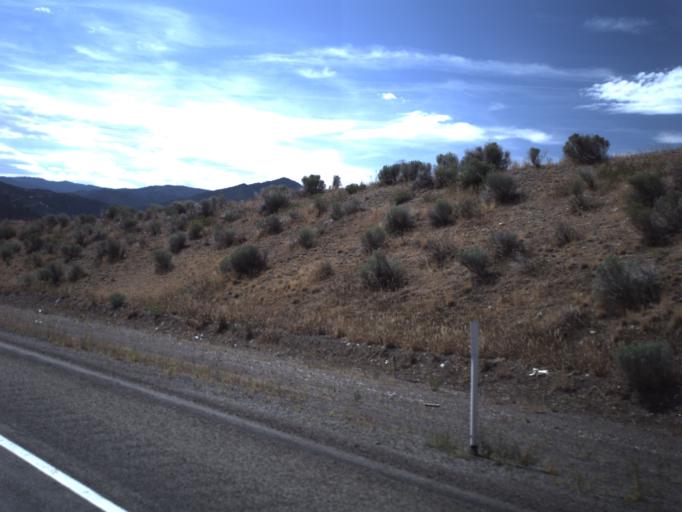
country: US
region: Utah
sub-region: Utah County
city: Mapleton
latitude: 40.0017
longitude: -111.4891
